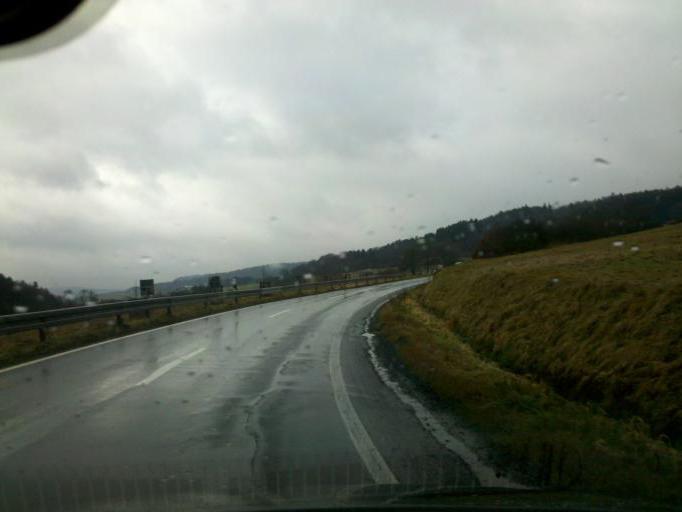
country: DE
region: Hesse
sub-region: Regierungsbezirk Giessen
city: Haiger
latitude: 50.7872
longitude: 8.2236
